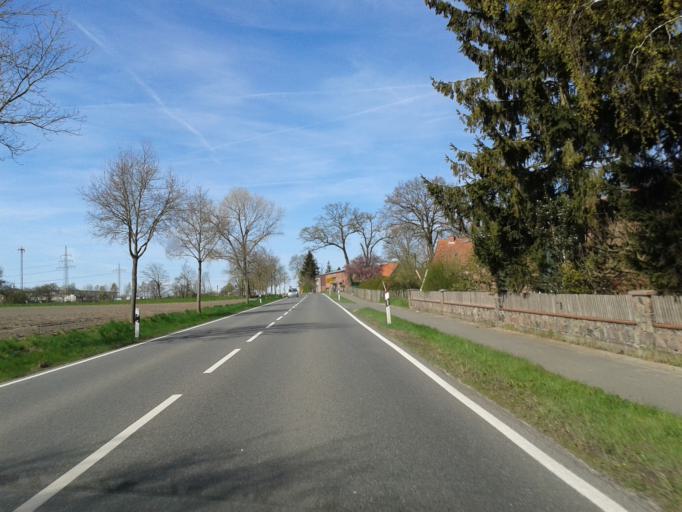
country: DE
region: Lower Saxony
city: Gerdau
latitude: 52.9612
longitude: 10.4597
